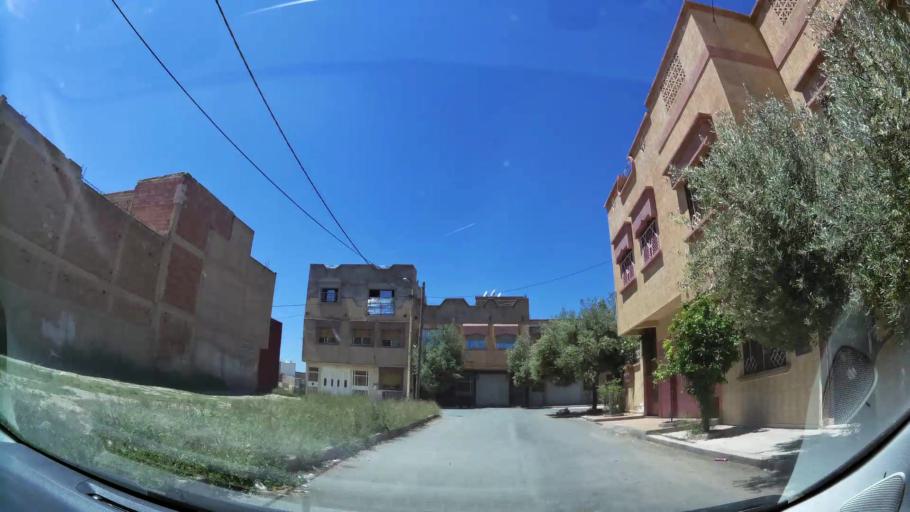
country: MA
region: Oriental
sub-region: Oujda-Angad
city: Oujda
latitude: 34.6771
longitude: -1.8657
